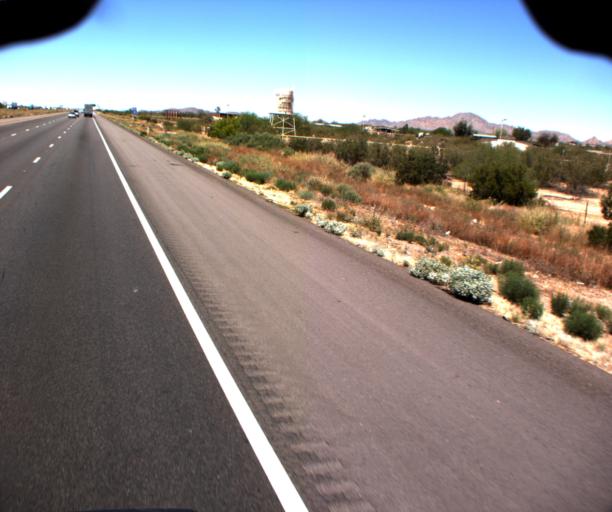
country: US
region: Arizona
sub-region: Pinal County
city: Casa Grande
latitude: 32.9447
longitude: -111.7058
